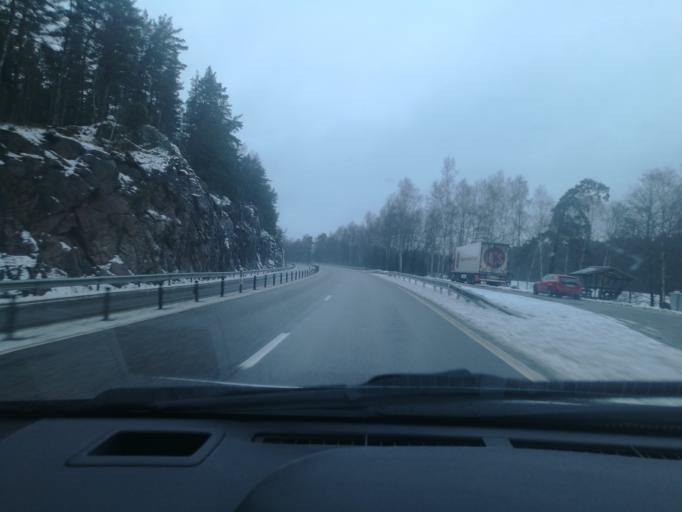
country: SE
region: OEstergoetland
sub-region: Norrkopings Kommun
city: Jursla
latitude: 58.7501
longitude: 16.1765
